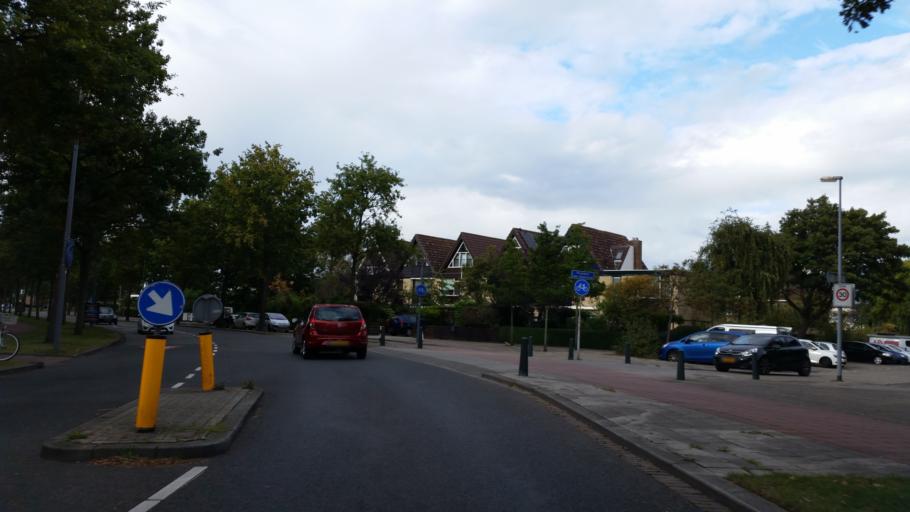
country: NL
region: South Holland
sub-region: Gemeente Rotterdam
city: Hoek van Holland
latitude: 51.9829
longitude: 4.1316
